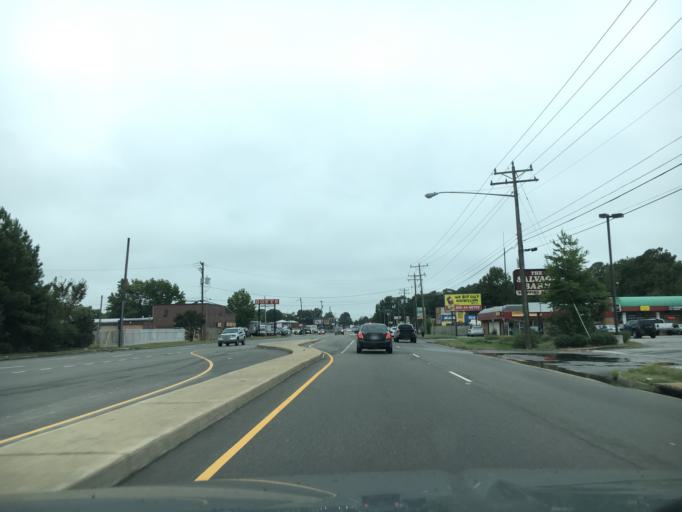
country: US
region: Virginia
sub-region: Chesterfield County
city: Bensley
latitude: 37.4923
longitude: -77.4891
